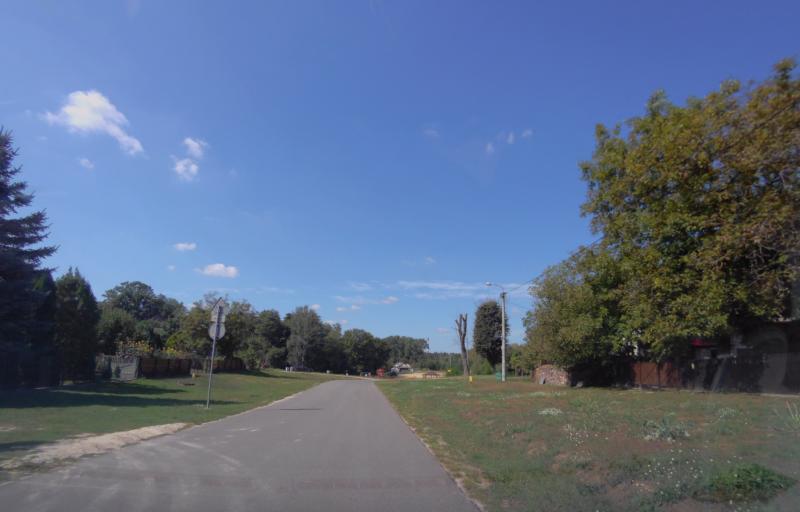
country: PL
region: Subcarpathian Voivodeship
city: Nowa Sarzyna
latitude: 50.3135
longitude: 22.3390
